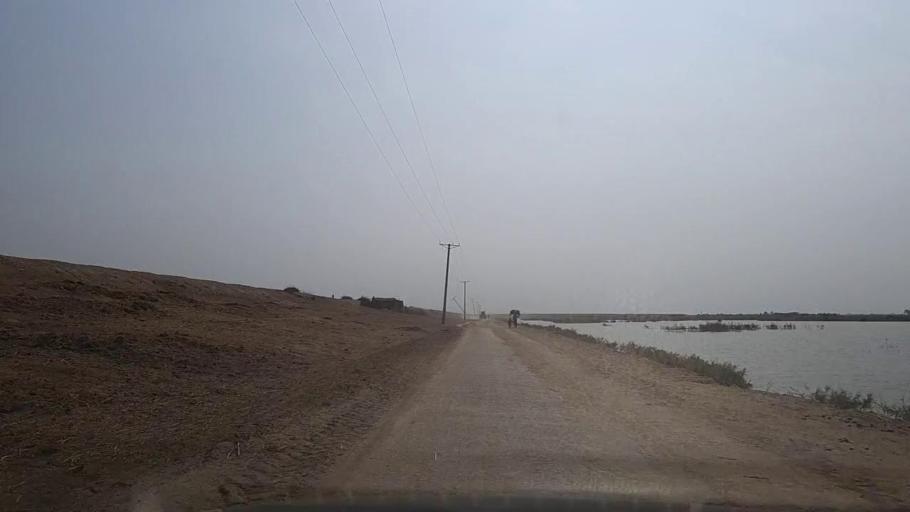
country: PK
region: Sindh
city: Thatta
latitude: 24.5807
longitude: 67.9151
